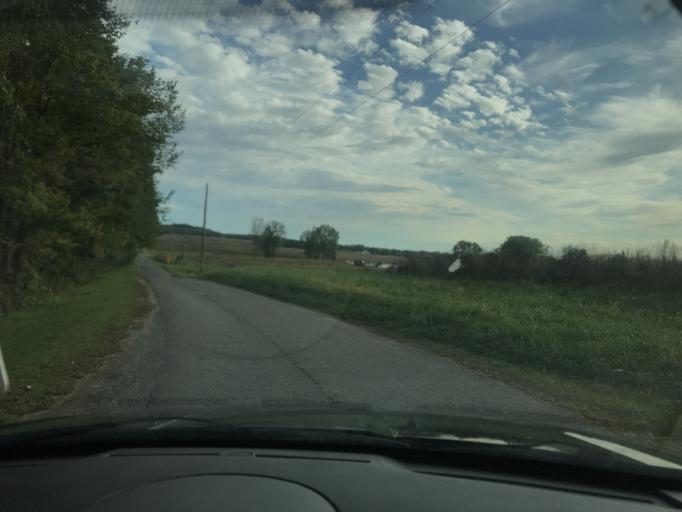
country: US
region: Ohio
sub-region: Logan County
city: West Liberty
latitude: 40.2221
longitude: -83.6757
